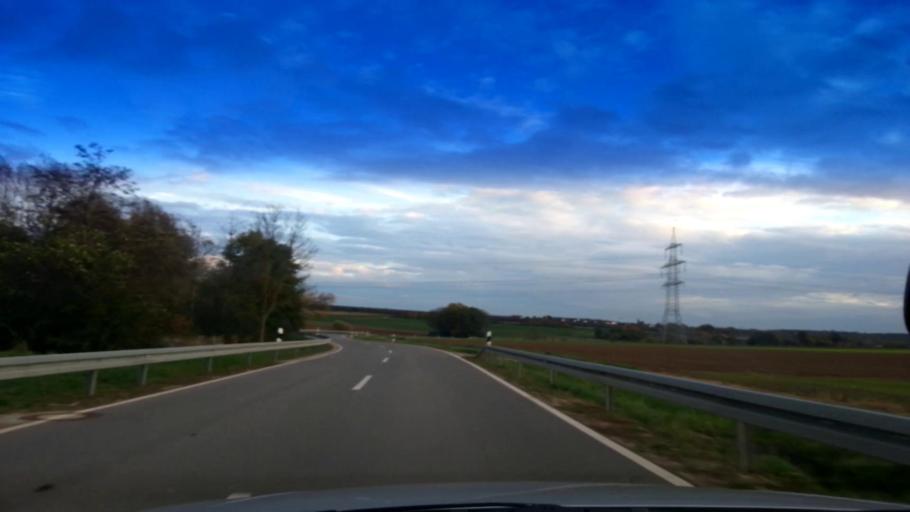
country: DE
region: Bavaria
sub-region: Upper Franconia
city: Memmelsdorf
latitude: 49.9554
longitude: 10.9645
